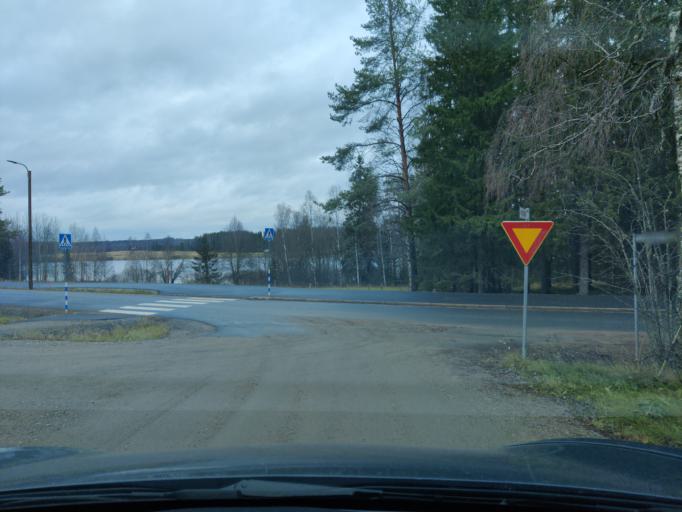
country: FI
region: Northern Savo
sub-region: Ylae-Savo
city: Kiuruvesi
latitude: 63.6464
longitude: 26.6404
